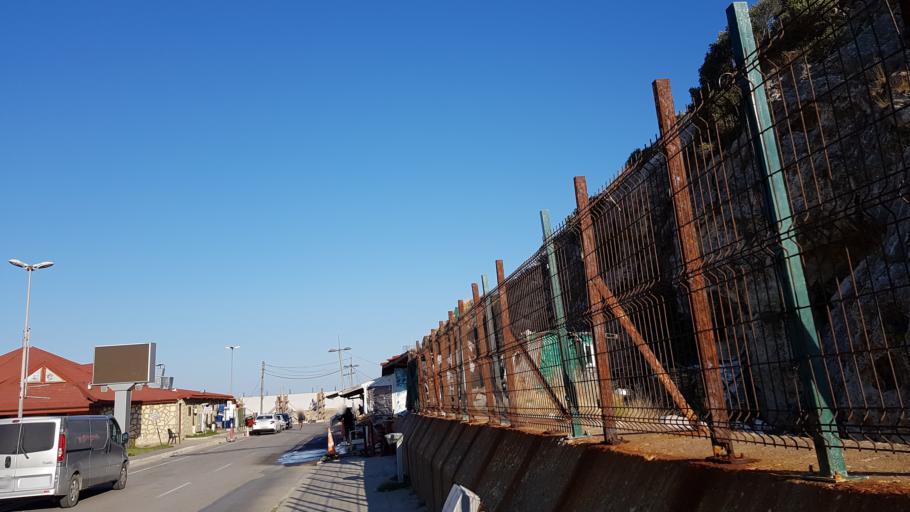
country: TR
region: Istanbul
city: Sile
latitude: 41.1811
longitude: 29.6075
